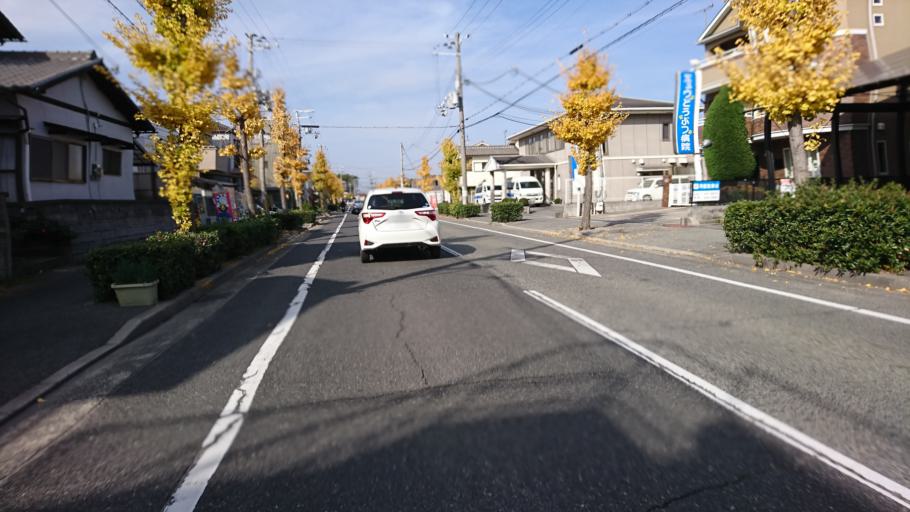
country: JP
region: Hyogo
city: Kakogawacho-honmachi
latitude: 34.7362
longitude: 134.8387
